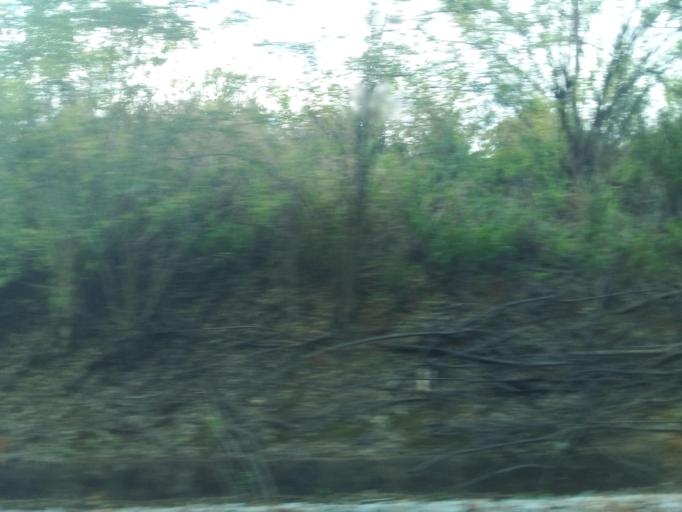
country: BR
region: Minas Gerais
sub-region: Governador Valadares
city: Governador Valadares
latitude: -18.9158
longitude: -42.0080
